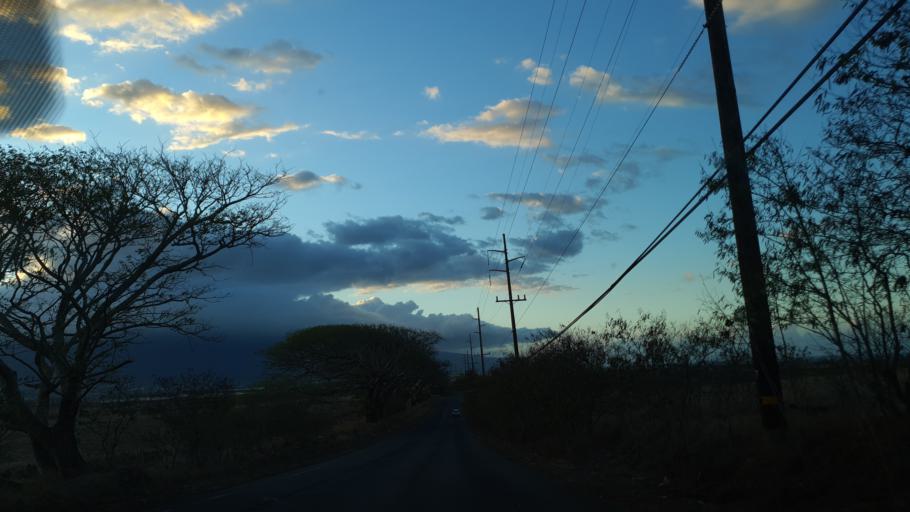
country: US
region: Hawaii
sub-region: Maui County
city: Kahului
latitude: 20.8656
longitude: -156.4321
